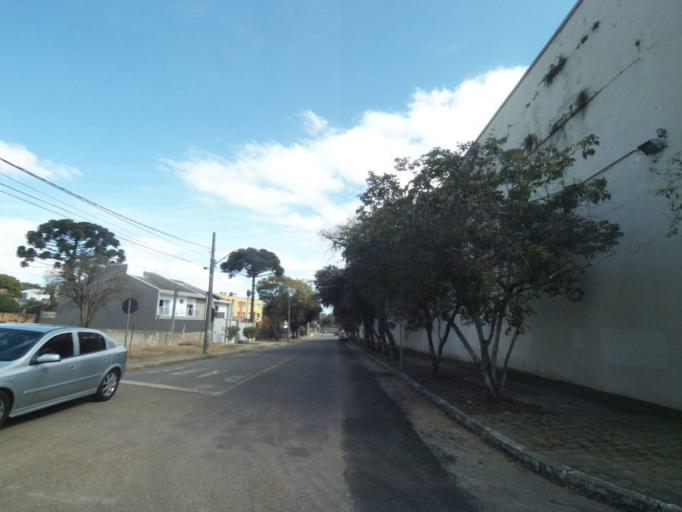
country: BR
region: Parana
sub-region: Curitiba
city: Curitiba
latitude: -25.4673
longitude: -49.2837
